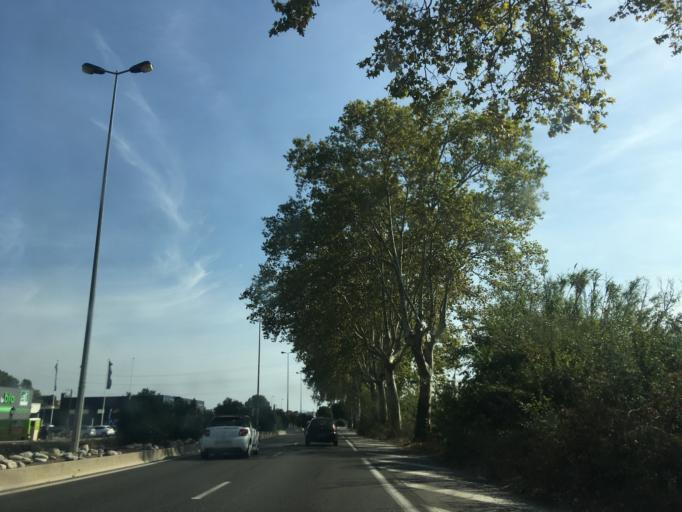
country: FR
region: Provence-Alpes-Cote d'Azur
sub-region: Departement du Var
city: Trans-en-Provence
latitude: 43.5106
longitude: 6.4798
